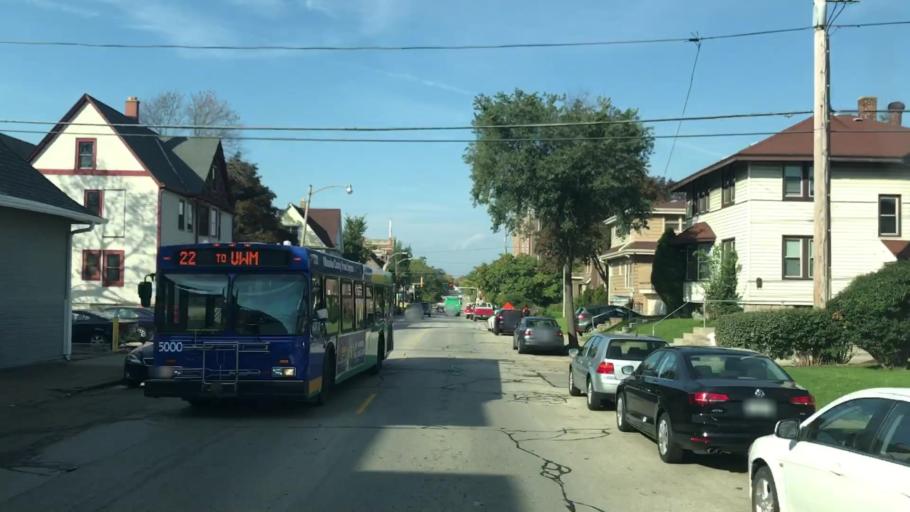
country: US
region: Wisconsin
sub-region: Milwaukee County
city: Shorewood
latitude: 43.0711
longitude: -87.8858
